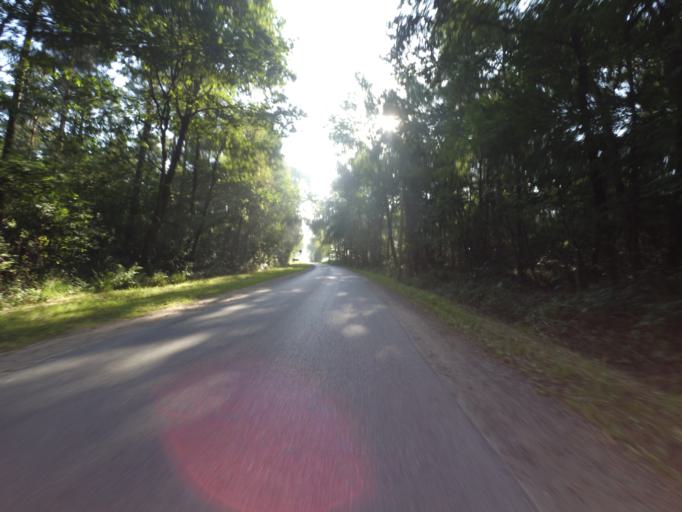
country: DE
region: Lower Saxony
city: Suddendorf
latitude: 52.2787
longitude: 7.2211
